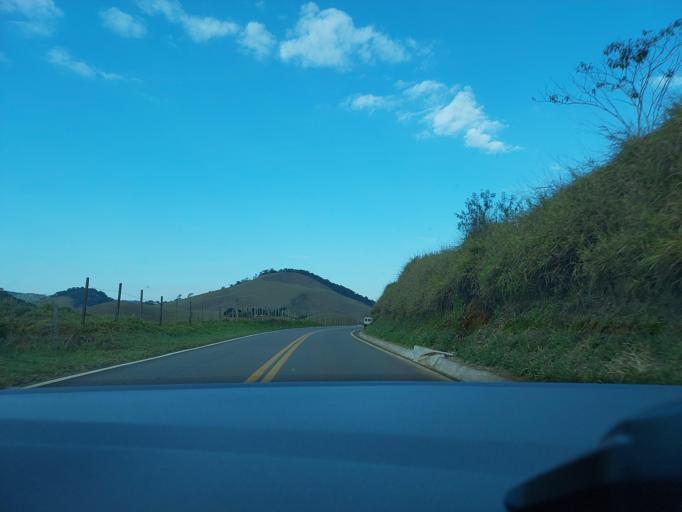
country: BR
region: Minas Gerais
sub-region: Muriae
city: Muriae
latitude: -21.0536
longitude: -42.5095
